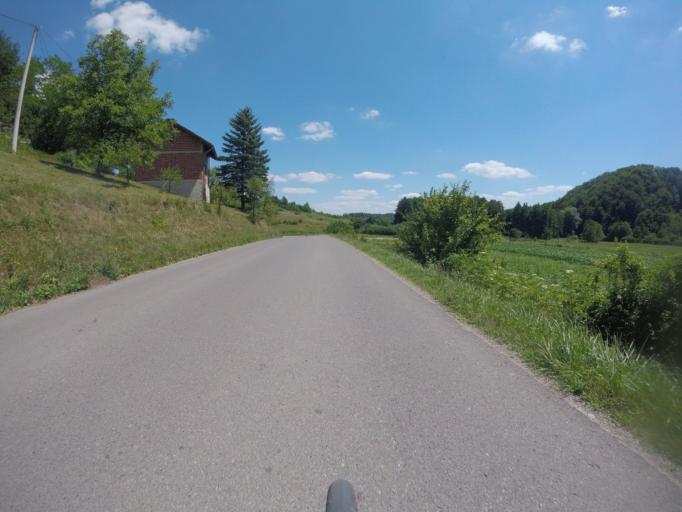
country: HR
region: Karlovacka
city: Ozalj
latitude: 45.6627
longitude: 15.4942
